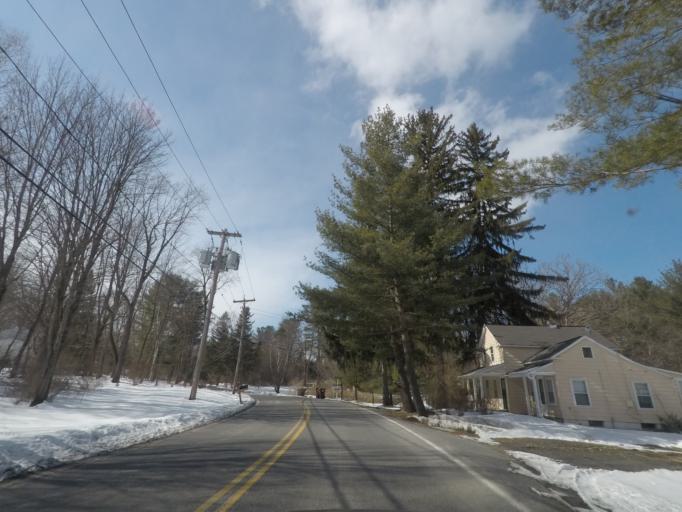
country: US
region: New York
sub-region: Albany County
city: Delmar
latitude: 42.6326
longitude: -73.8734
